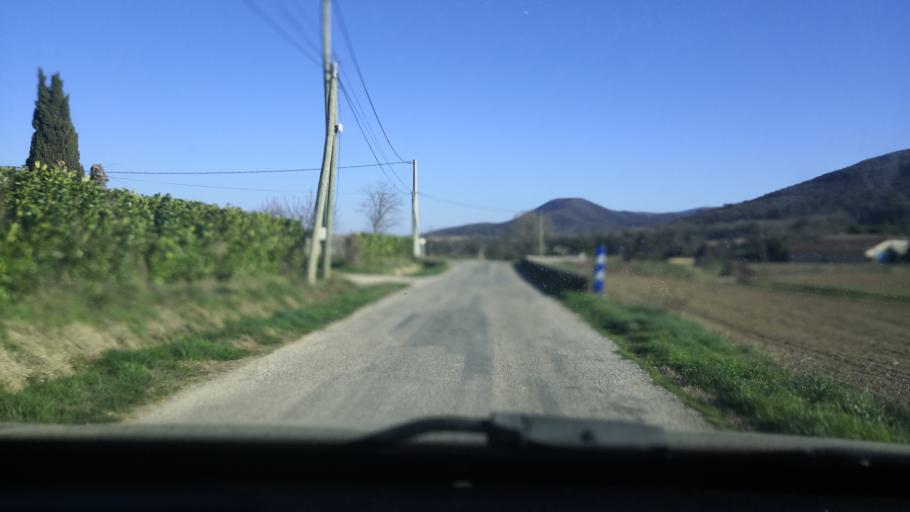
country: FR
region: Rhone-Alpes
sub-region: Departement de la Drome
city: Savasse
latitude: 44.6240
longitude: 4.7887
